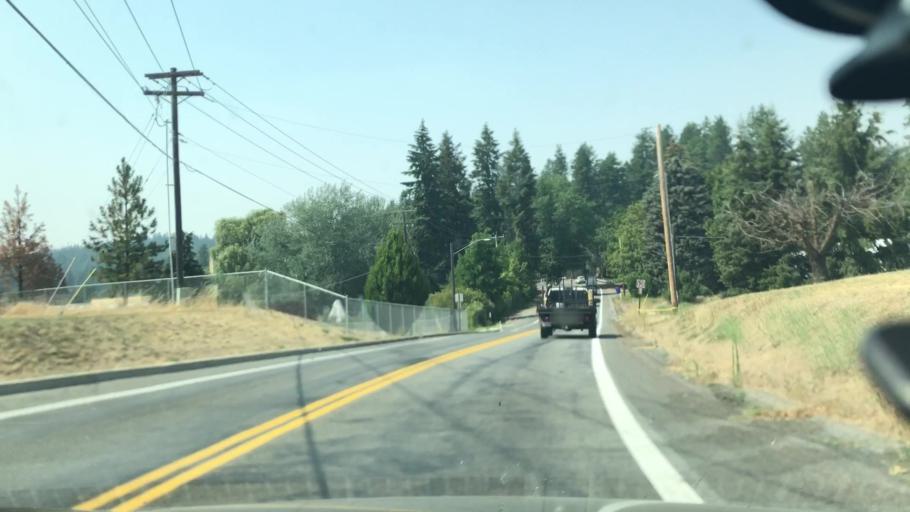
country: US
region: Washington
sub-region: Spokane County
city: Millwood
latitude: 47.6971
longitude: -117.2862
